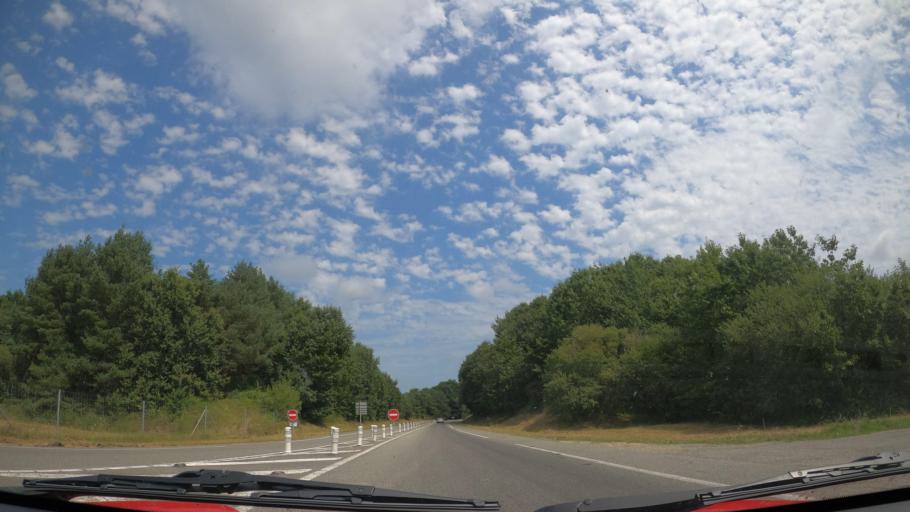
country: FR
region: Aquitaine
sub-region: Departement des Landes
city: Peyrehorade
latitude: 43.5189
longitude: -1.1064
